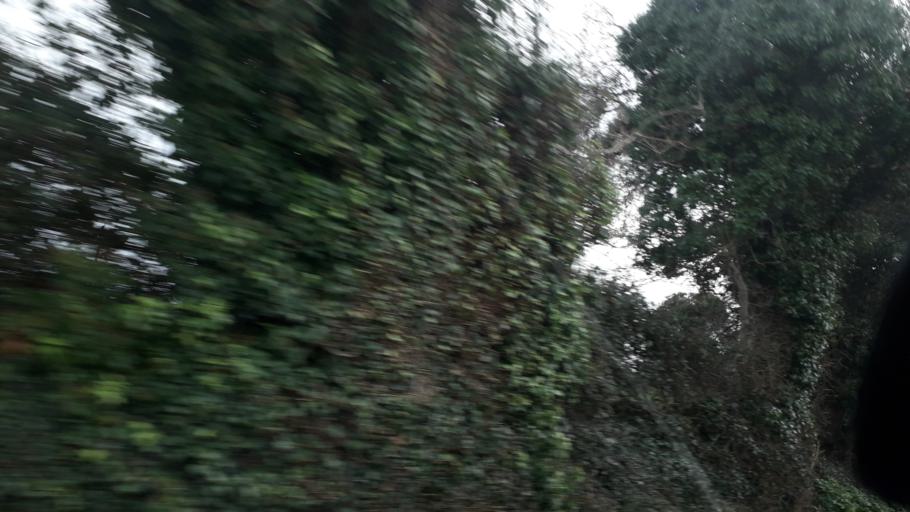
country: IE
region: Ulster
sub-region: County Donegal
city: Buncrana
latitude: 55.1016
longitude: -7.5348
